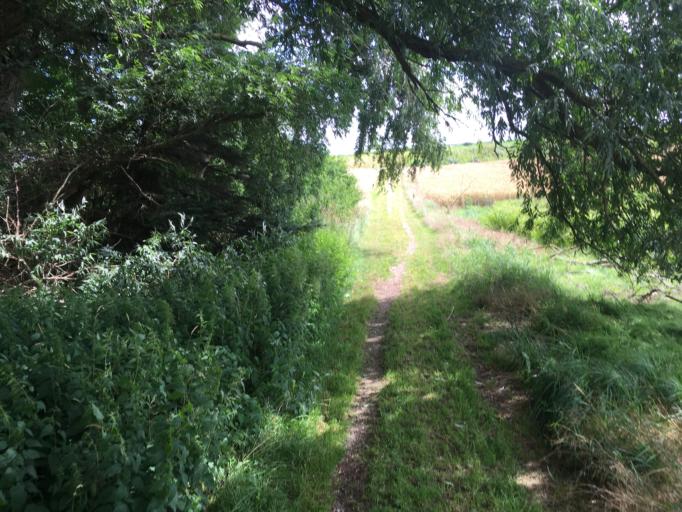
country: DK
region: Capital Region
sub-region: Fredensborg Kommune
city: Niva
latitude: 55.9315
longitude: 12.4771
